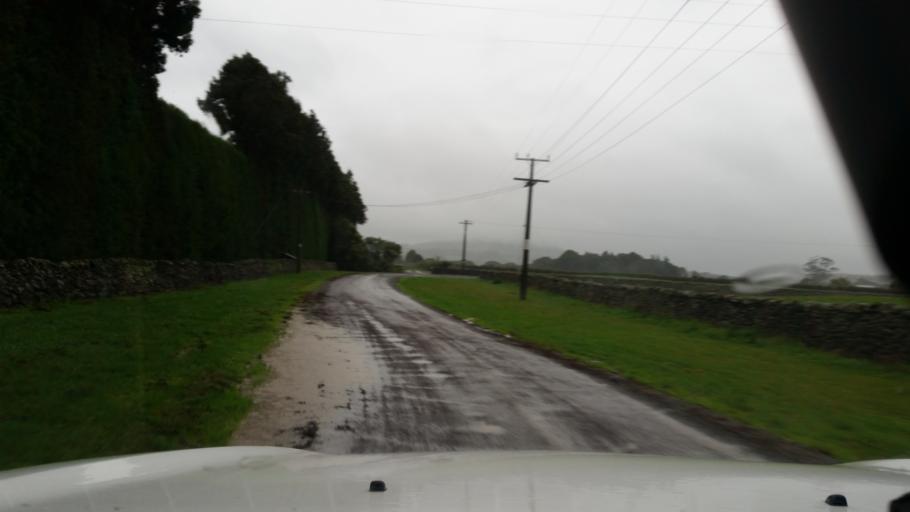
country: NZ
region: Northland
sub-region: Whangarei
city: Maungatapere
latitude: -35.7520
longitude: 174.1807
